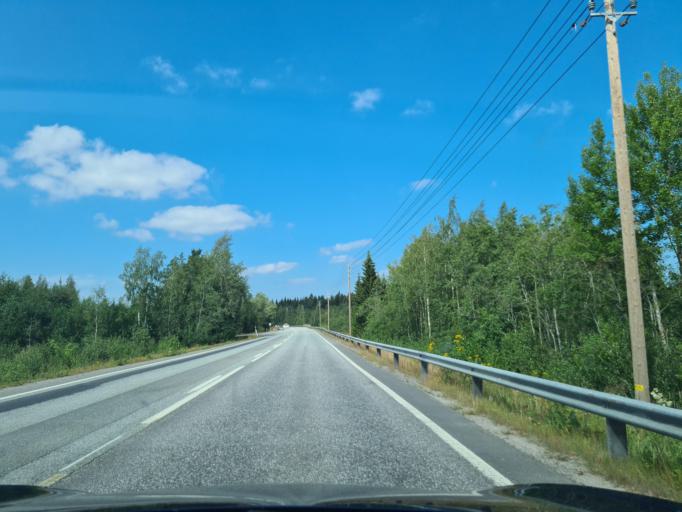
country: FI
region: Ostrobothnia
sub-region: Vaasa
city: Vaasa
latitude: 63.1873
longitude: 21.5659
